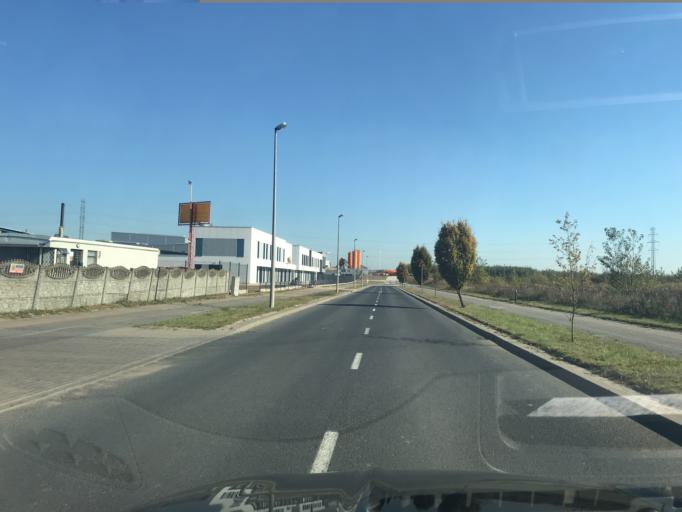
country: PL
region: Warmian-Masurian Voivodeship
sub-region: Powiat ilawski
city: Lubawa
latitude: 53.5167
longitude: 19.7315
